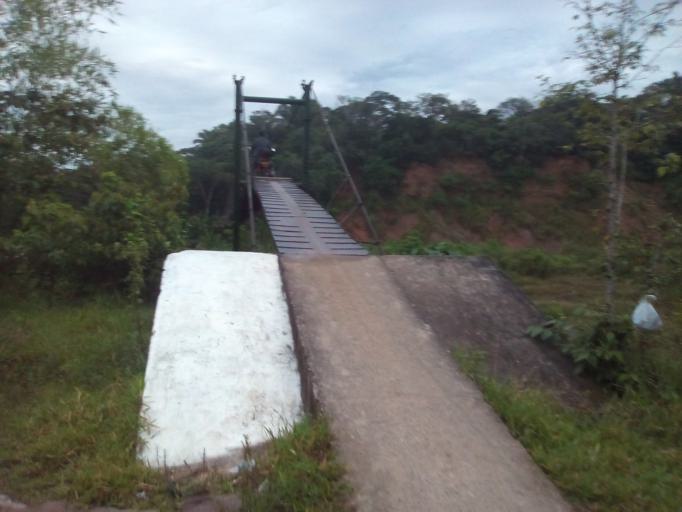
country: CO
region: Casanare
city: Nunchia
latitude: 5.6321
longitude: -72.2023
